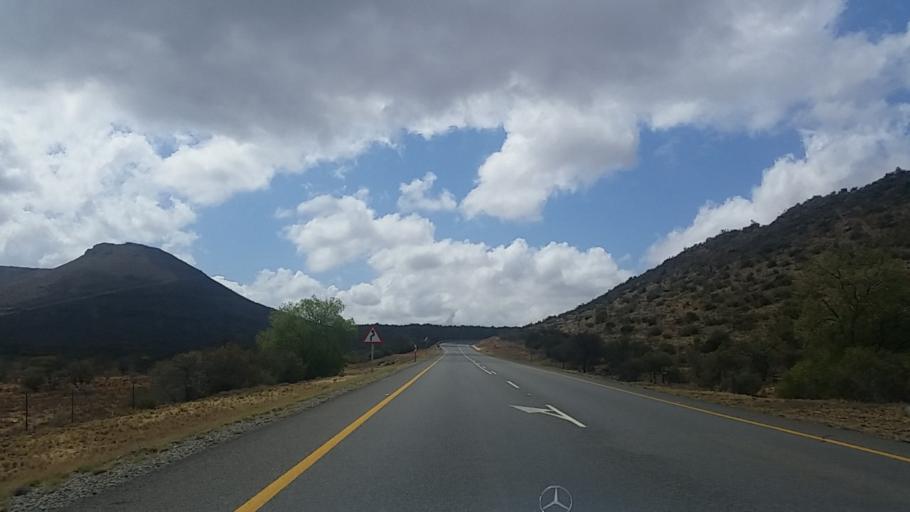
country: ZA
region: Eastern Cape
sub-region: Cacadu District Municipality
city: Graaff-Reinet
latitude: -32.0656
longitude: 24.6062
